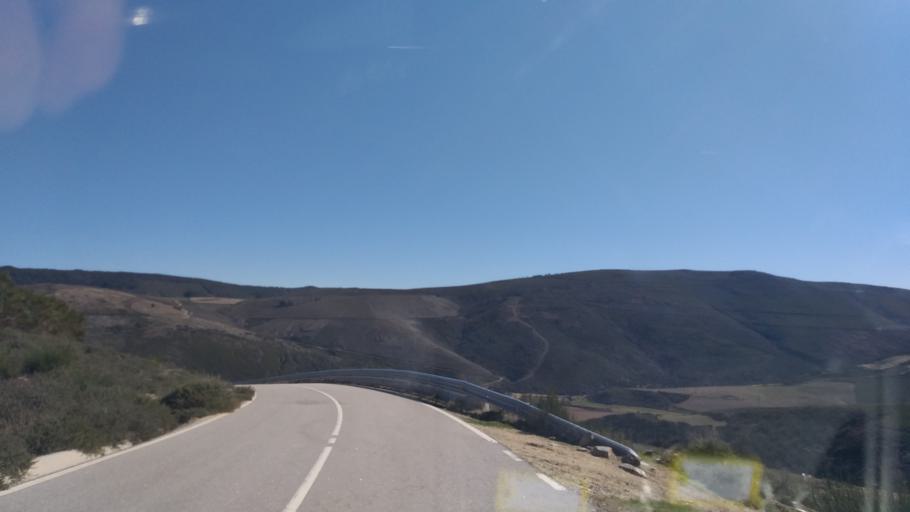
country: PT
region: Guarda
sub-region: Manteigas
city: Manteigas
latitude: 40.4633
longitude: -7.5030
